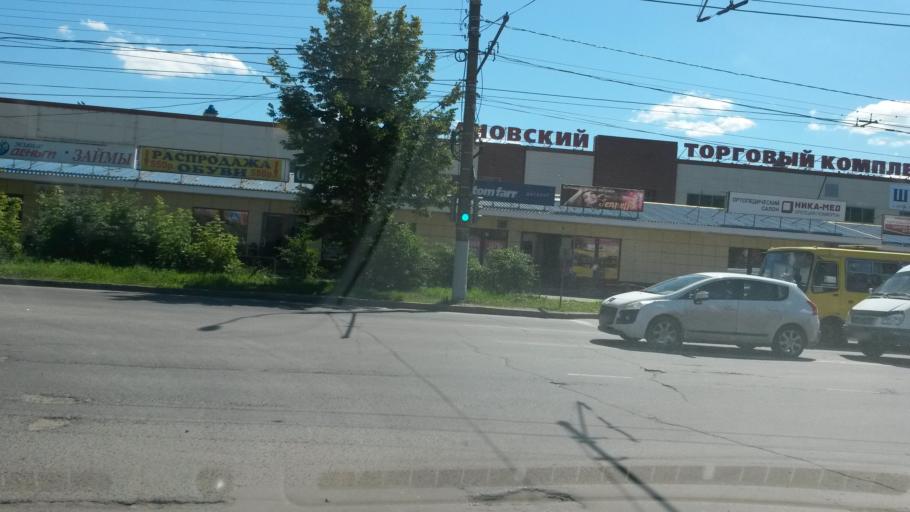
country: RU
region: Ivanovo
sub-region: Gorod Ivanovo
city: Ivanovo
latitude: 56.9886
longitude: 40.9678
